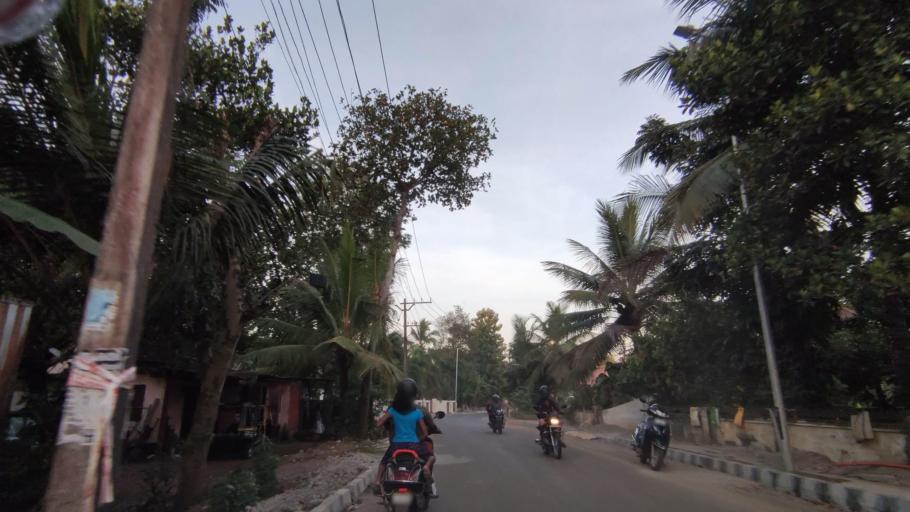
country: IN
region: Kerala
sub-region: Kottayam
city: Kottayam
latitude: 9.6423
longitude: 76.4984
